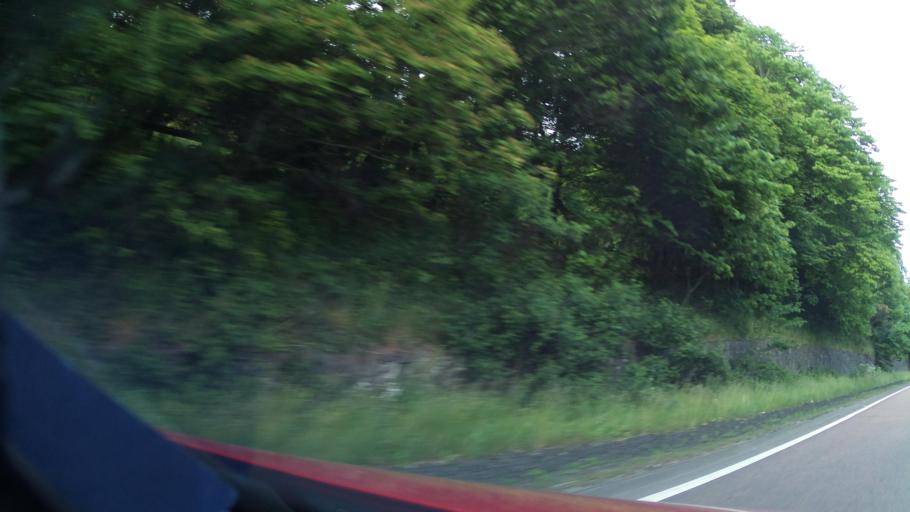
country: GB
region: Scotland
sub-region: Perth and Kinross
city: Scone
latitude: 56.3869
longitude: -3.3872
